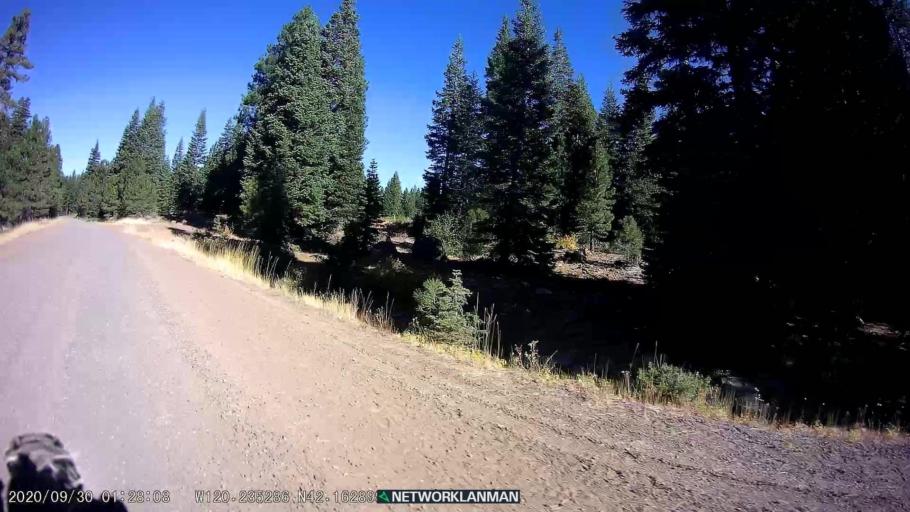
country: US
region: Oregon
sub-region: Lake County
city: Lakeview
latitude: 42.1660
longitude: -120.2398
